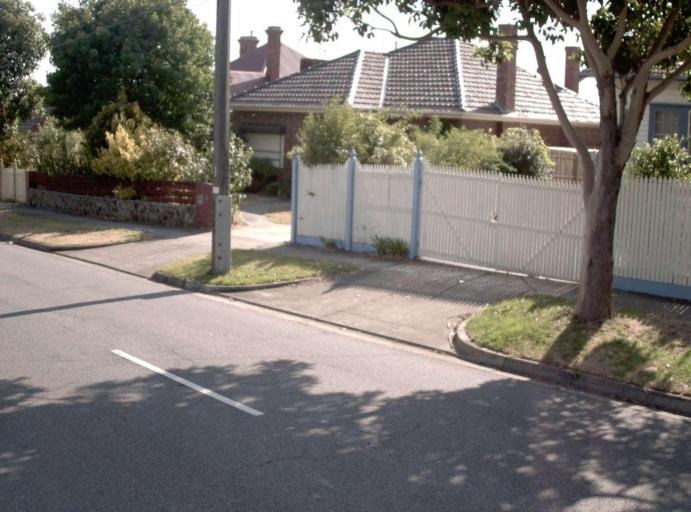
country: AU
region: Victoria
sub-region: Whitehorse
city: Box Hill North
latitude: -37.8101
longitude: 145.1254
